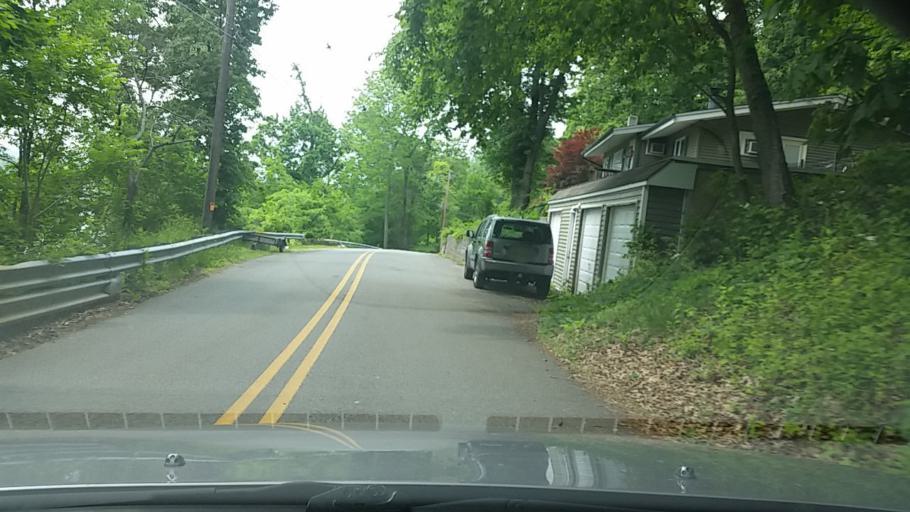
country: US
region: New Jersey
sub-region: Warren County
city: Oxford
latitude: 40.8628
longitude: -74.9850
